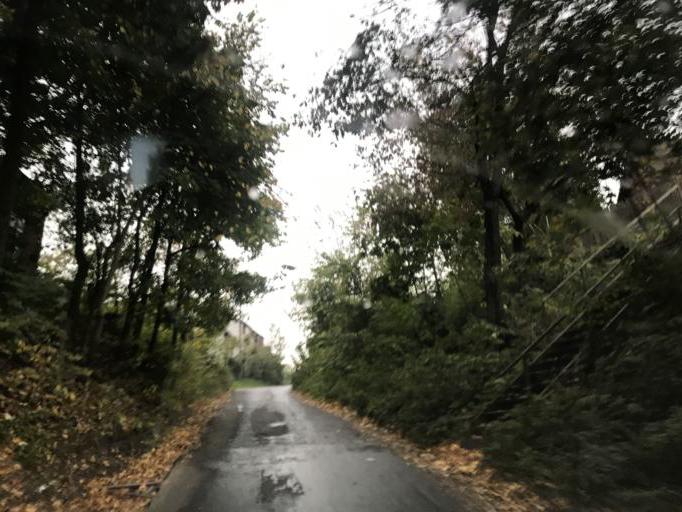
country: BY
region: Mogilev
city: Mahilyow
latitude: 53.8991
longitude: 30.3253
